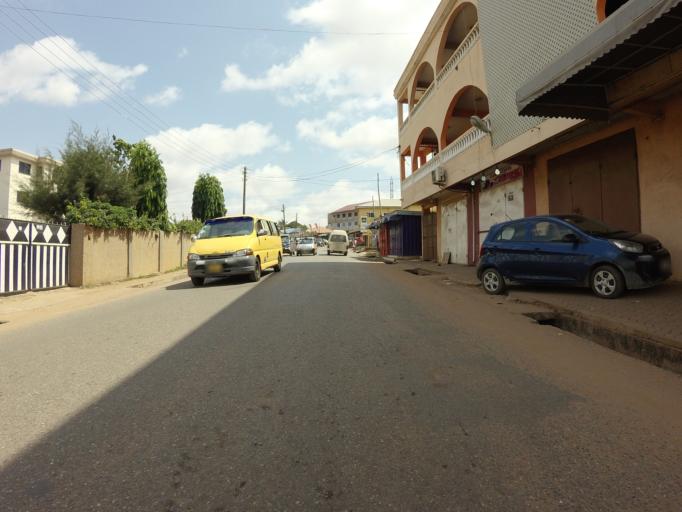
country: GH
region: Greater Accra
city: Dome
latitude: 5.6166
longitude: -0.2492
